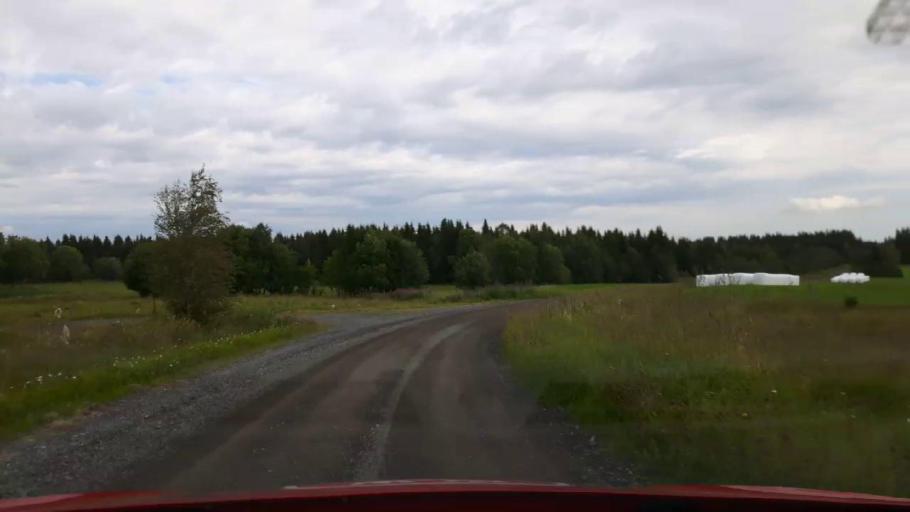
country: SE
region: Jaemtland
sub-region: OEstersunds Kommun
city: Lit
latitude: 63.3823
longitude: 15.1949
